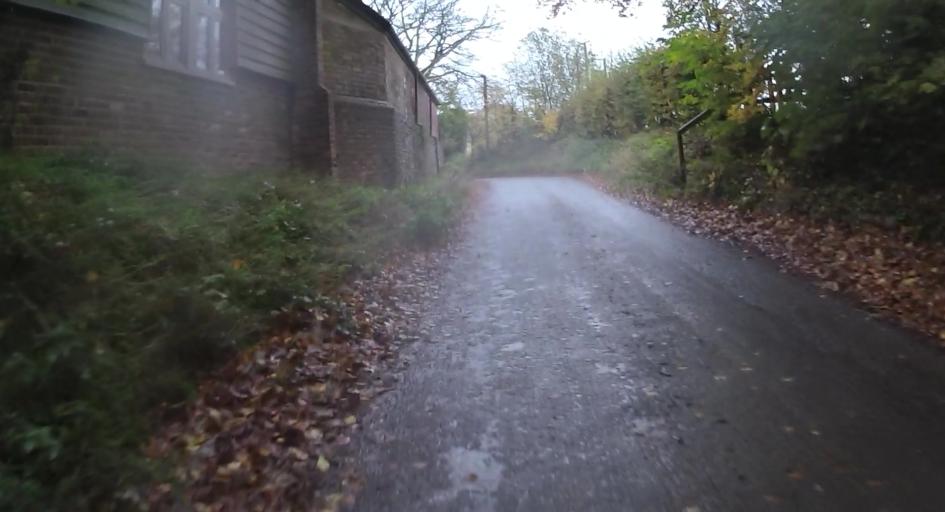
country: GB
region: England
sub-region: Hampshire
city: Four Marks
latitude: 51.1307
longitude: -1.0820
